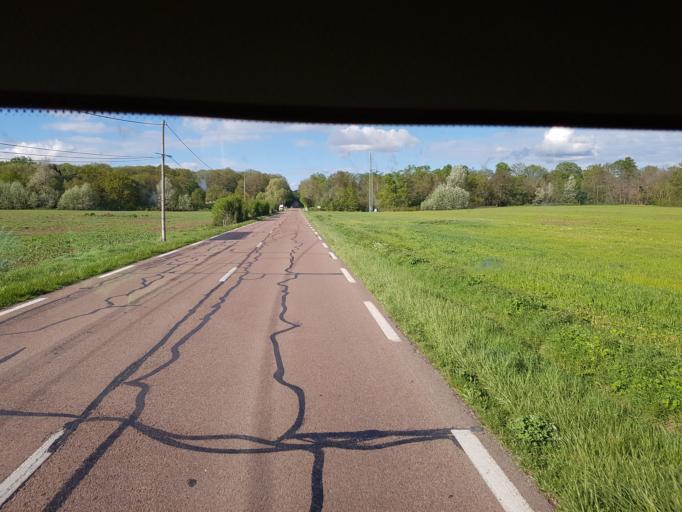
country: FR
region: Bourgogne
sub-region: Departement de l'Yonne
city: Vergigny
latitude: 47.9247
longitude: 3.7160
